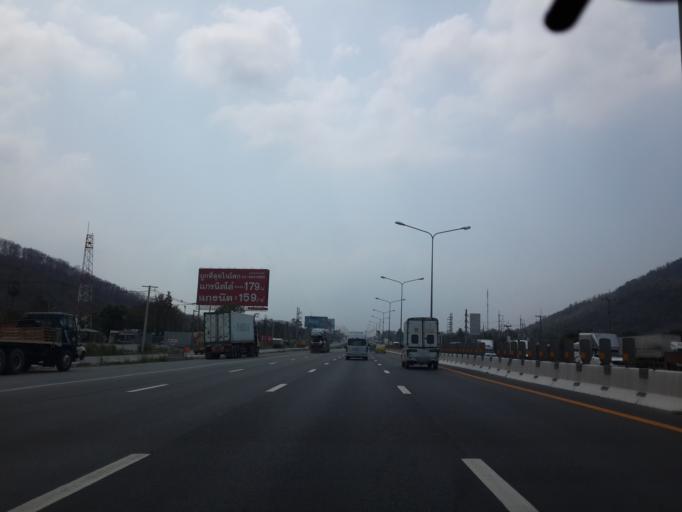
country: TH
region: Chon Buri
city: Chon Buri
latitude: 13.2786
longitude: 100.9907
